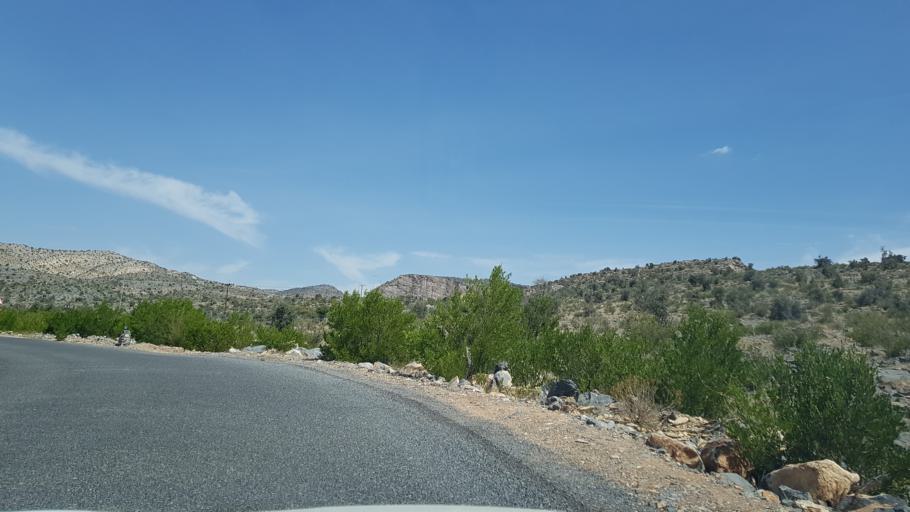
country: OM
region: Al Batinah
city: Bayt al `Awabi
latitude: 23.1404
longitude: 57.5393
